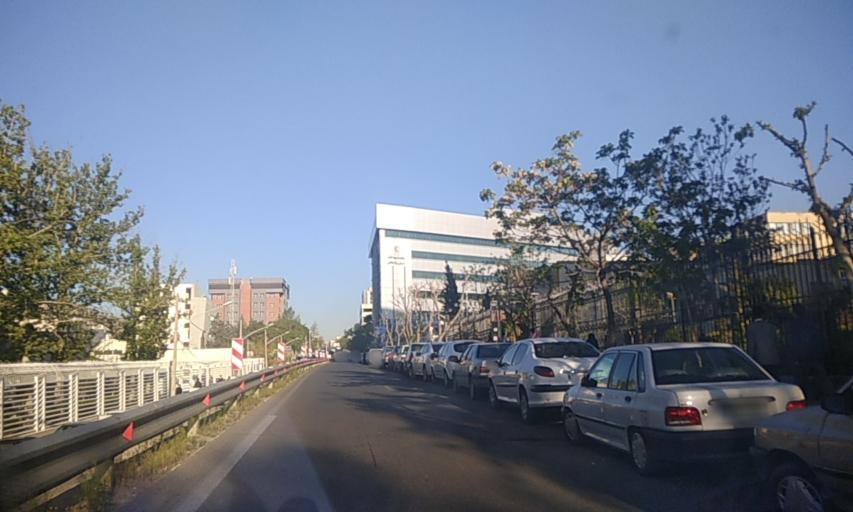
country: IR
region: Tehran
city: Tajrish
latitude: 35.7682
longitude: 51.4106
